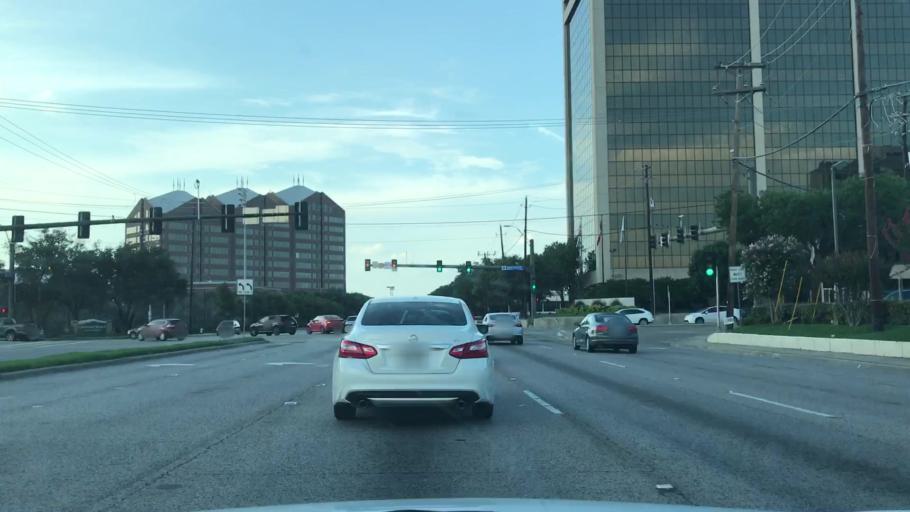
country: US
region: Texas
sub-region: Dallas County
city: Addison
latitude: 32.9394
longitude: -96.8389
